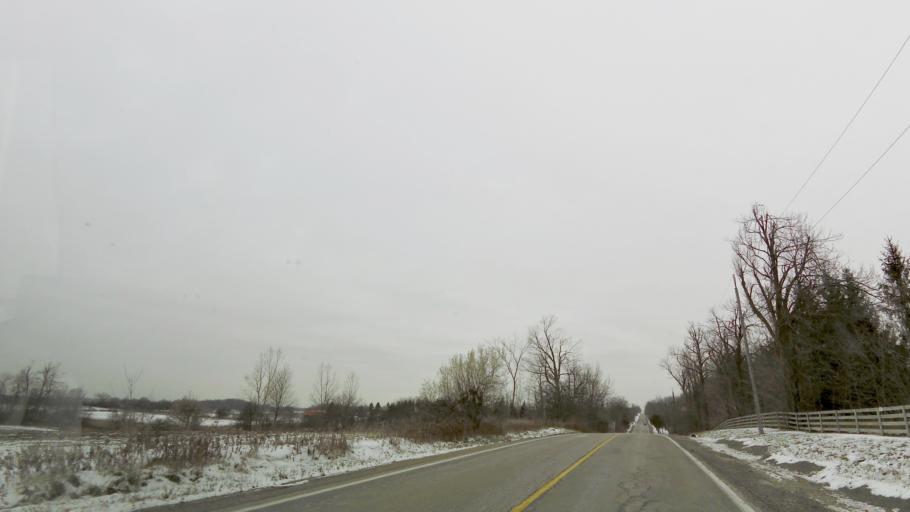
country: CA
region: Ontario
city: Vaughan
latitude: 43.8789
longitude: -79.5954
